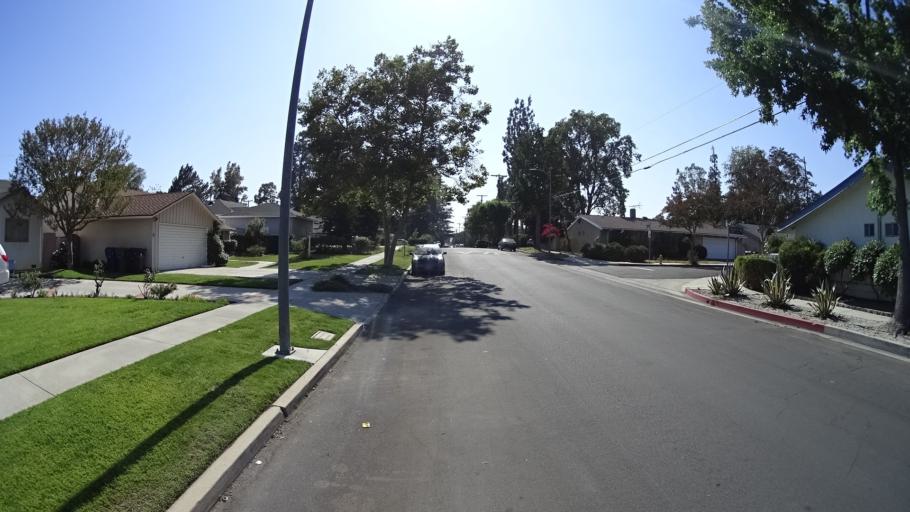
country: US
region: California
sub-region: Los Angeles County
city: Van Nuys
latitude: 34.1993
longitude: -118.4275
